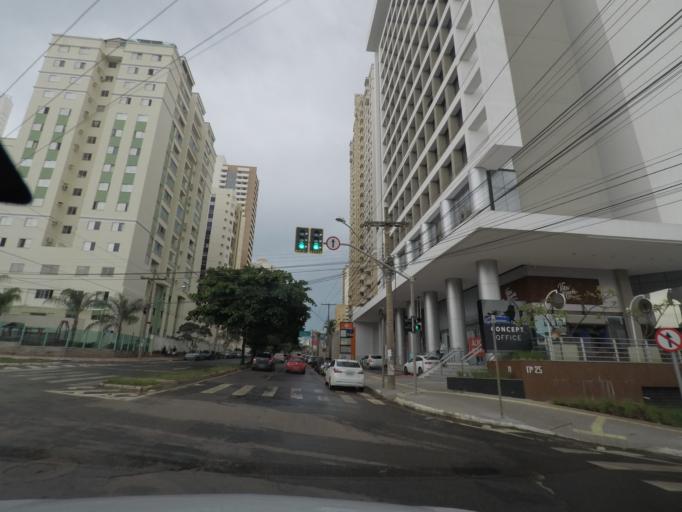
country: BR
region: Goias
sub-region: Goiania
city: Goiania
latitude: -16.7103
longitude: -49.2405
